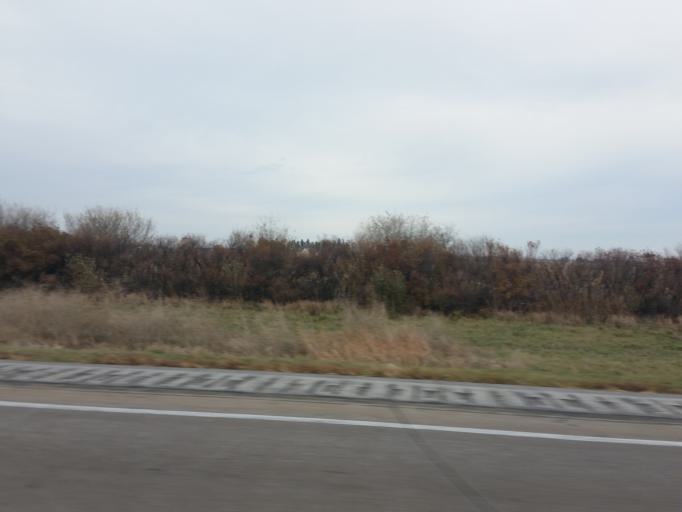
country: US
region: Iowa
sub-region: Scott County
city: Walcott
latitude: 41.6038
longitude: -90.7081
